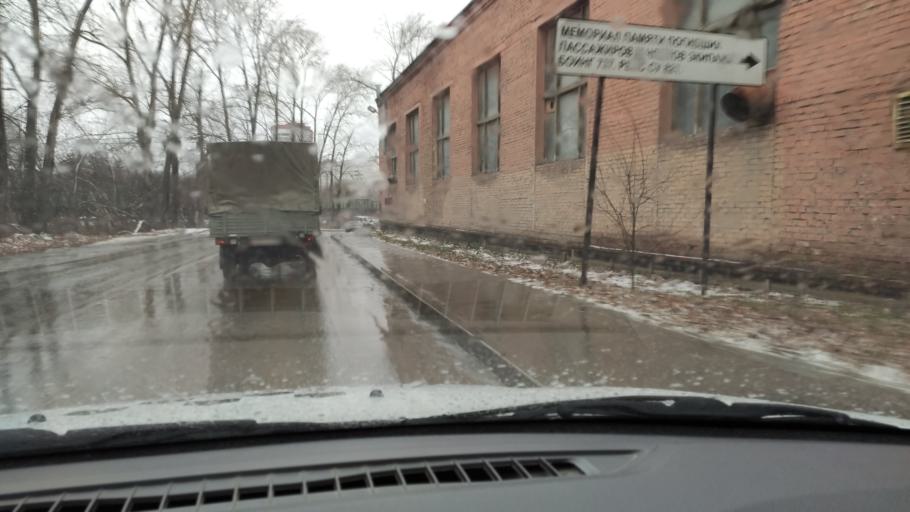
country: RU
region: Perm
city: Perm
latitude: 57.9600
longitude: 56.2072
